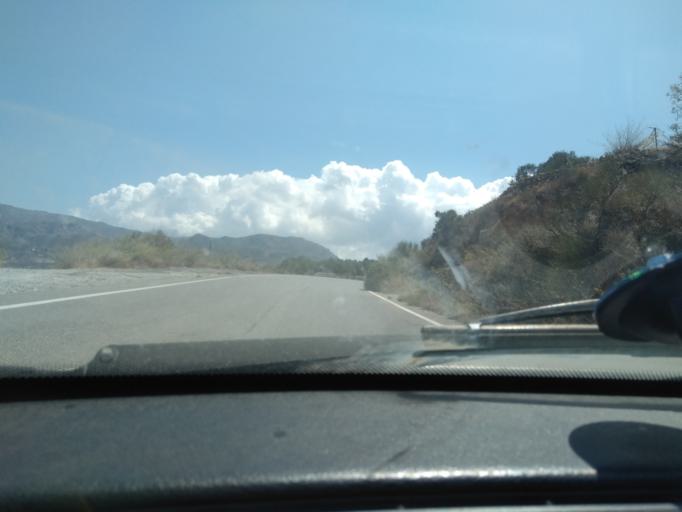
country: GR
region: Crete
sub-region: Nomos Lasithiou
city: Siteia
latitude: 35.1398
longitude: 26.0754
